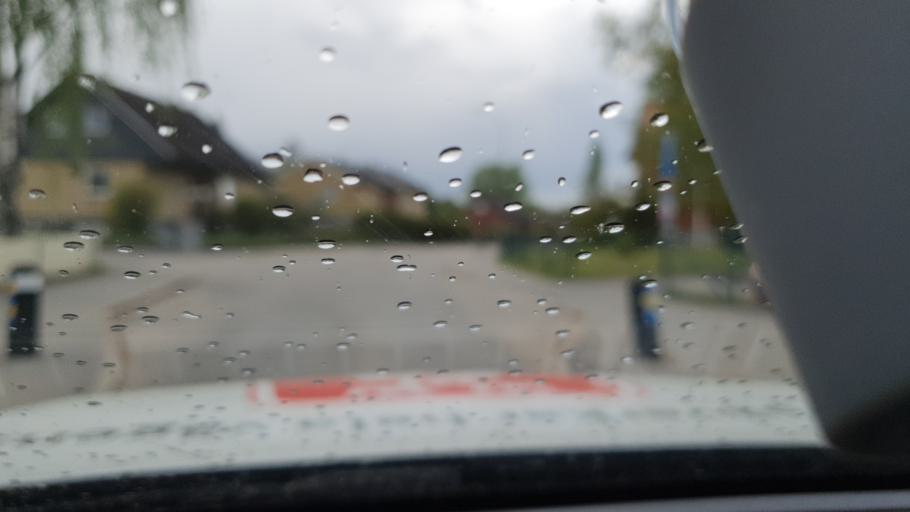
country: SE
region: Stockholm
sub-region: Huddinge Kommun
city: Huddinge
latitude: 59.2475
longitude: 17.9769
